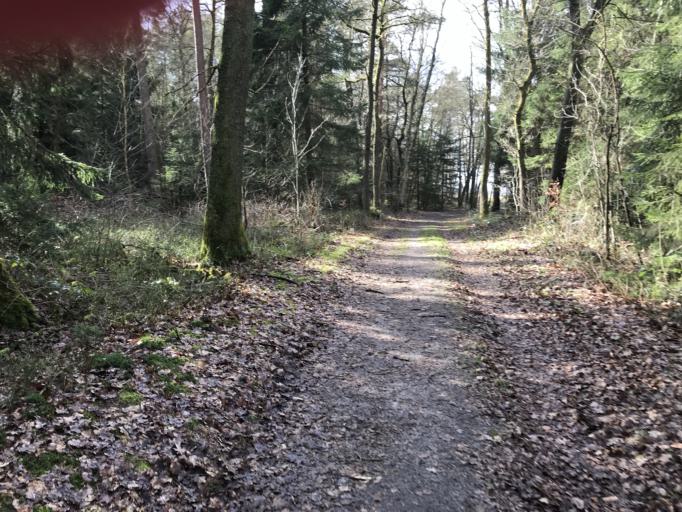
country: DE
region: Lower Saxony
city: Suderburg
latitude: 52.8865
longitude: 10.4341
